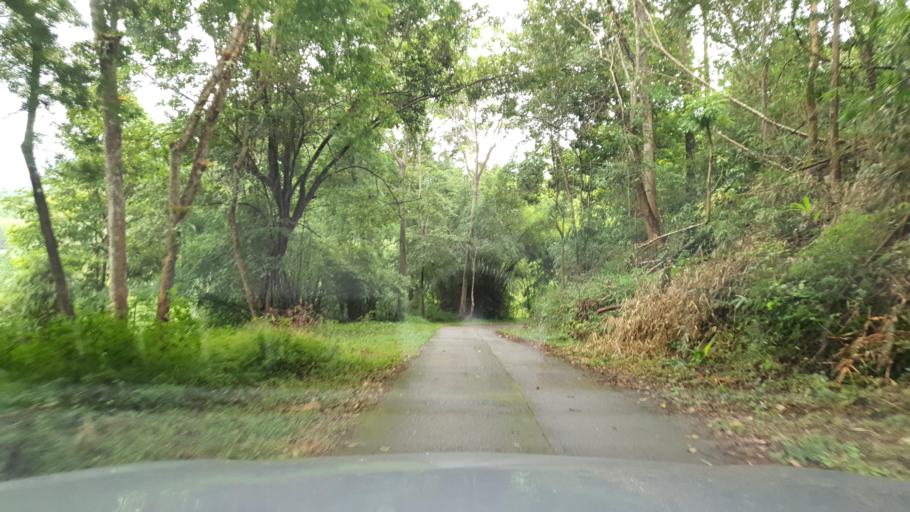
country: TH
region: Chiang Mai
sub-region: Amphoe Chiang Dao
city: Chiang Dao
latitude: 19.2733
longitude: 98.9469
